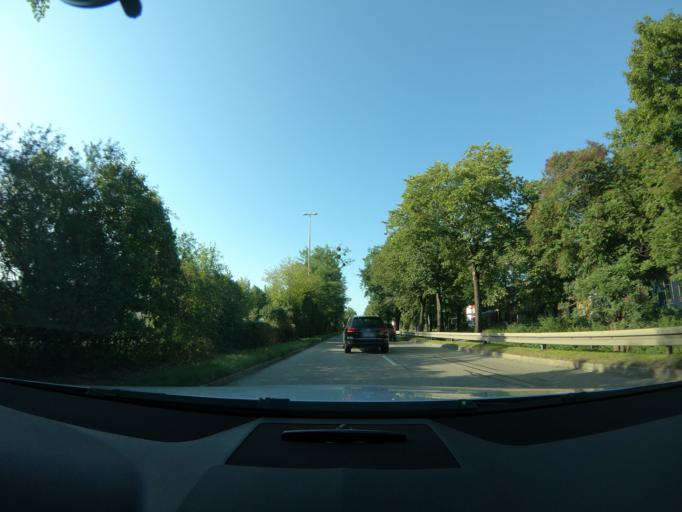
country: DE
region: Bavaria
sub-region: Upper Bavaria
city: Bogenhausen
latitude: 48.1919
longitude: 11.5842
